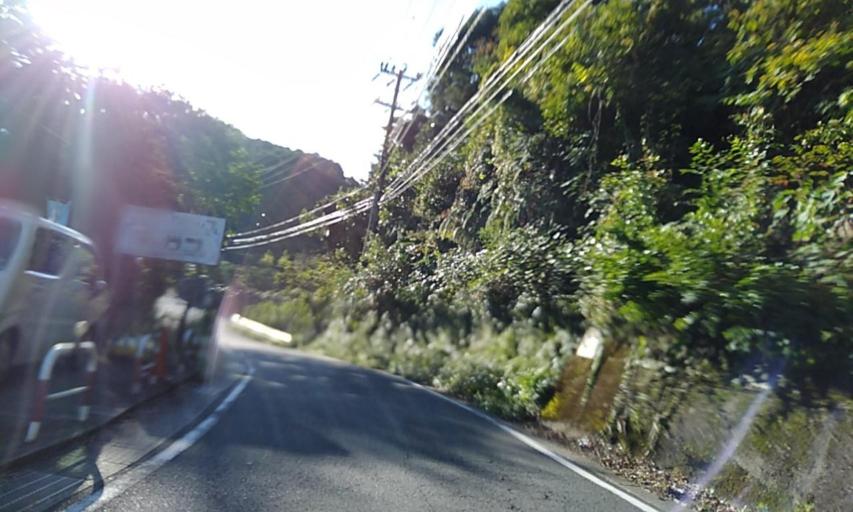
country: JP
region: Wakayama
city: Iwade
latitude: 34.1548
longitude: 135.3059
